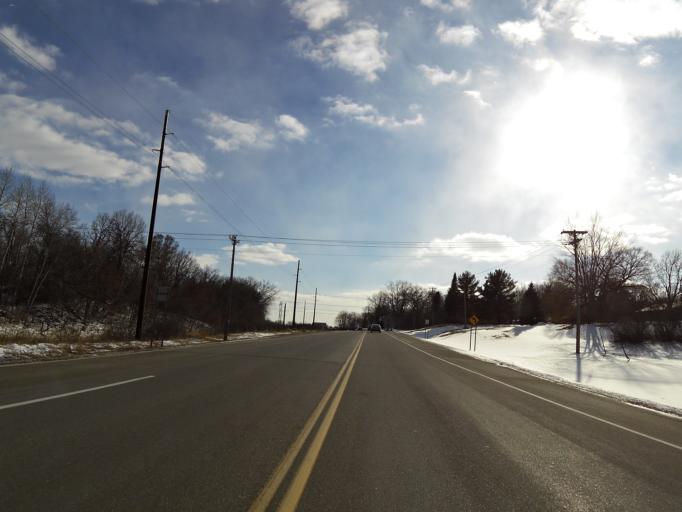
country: US
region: Minnesota
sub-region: Dakota County
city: Eagan
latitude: 44.8005
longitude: -93.1063
